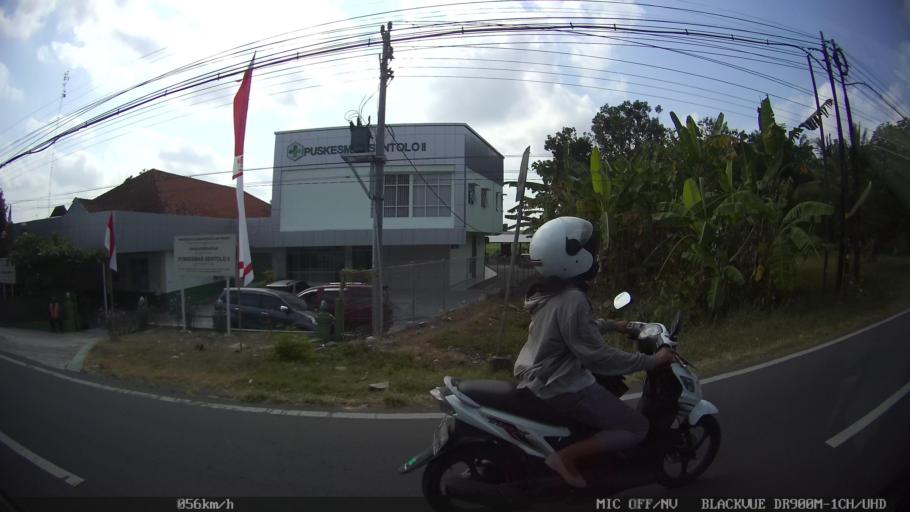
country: ID
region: Daerah Istimewa Yogyakarta
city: Srandakan
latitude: -7.8479
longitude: 110.2177
